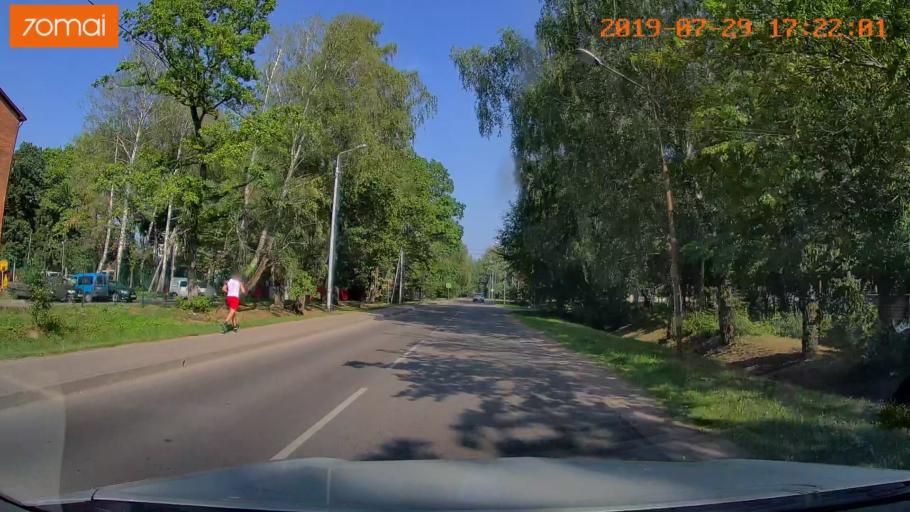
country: RU
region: Kaliningrad
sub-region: Gorod Kaliningrad
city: Kaliningrad
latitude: 54.7698
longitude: 20.4369
